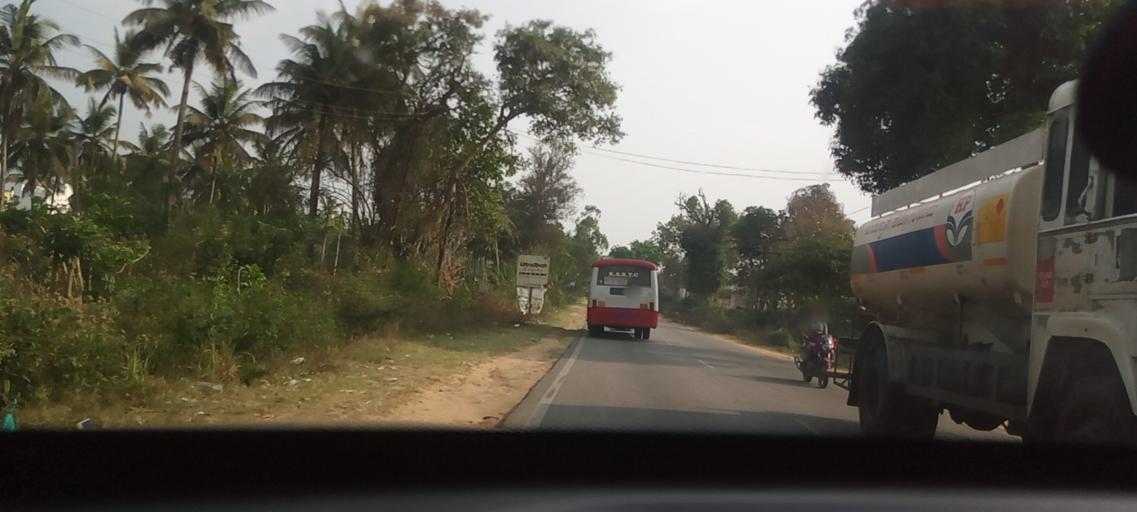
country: IN
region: Karnataka
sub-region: Hassan
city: Hassan
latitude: 13.0121
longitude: 76.0695
